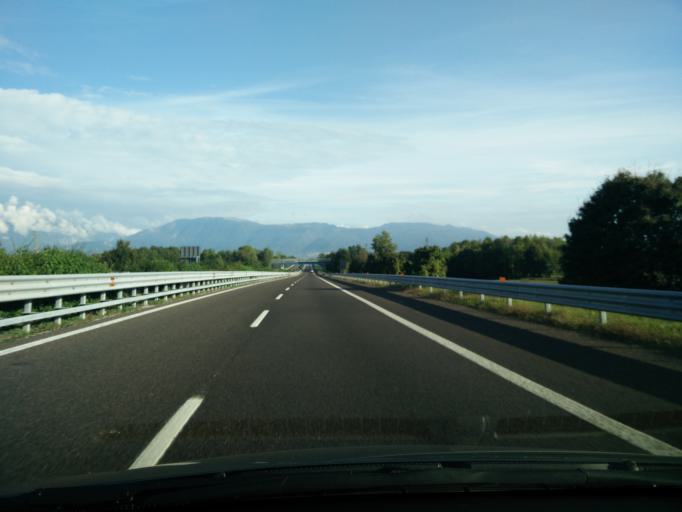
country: IT
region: Veneto
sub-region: Provincia di Treviso
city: San Vendemiano
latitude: 45.8890
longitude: 12.3413
